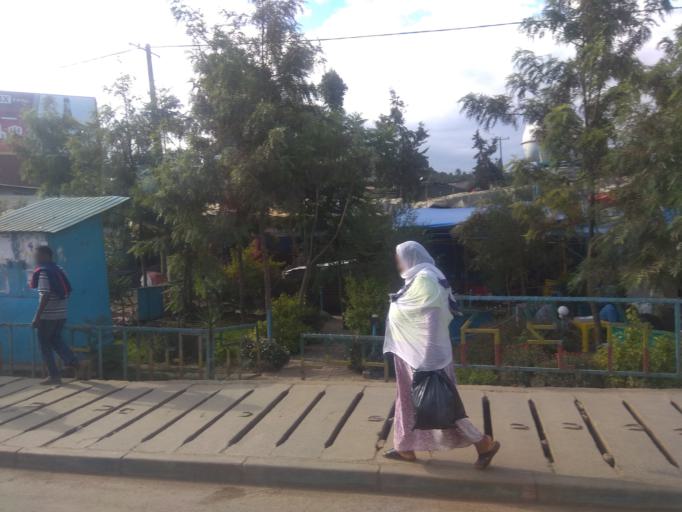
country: ET
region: Adis Abeba
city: Addis Ababa
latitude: 9.0335
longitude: 38.7125
